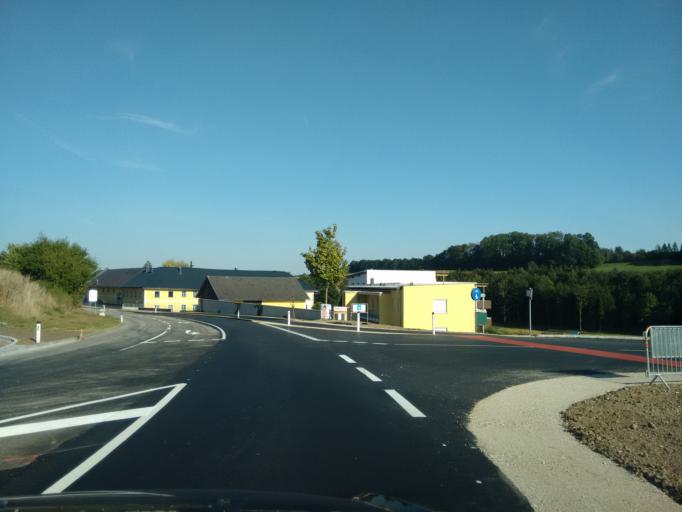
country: AT
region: Upper Austria
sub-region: Politischer Bezirk Linz-Land
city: Traun
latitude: 48.1427
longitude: 14.2122
